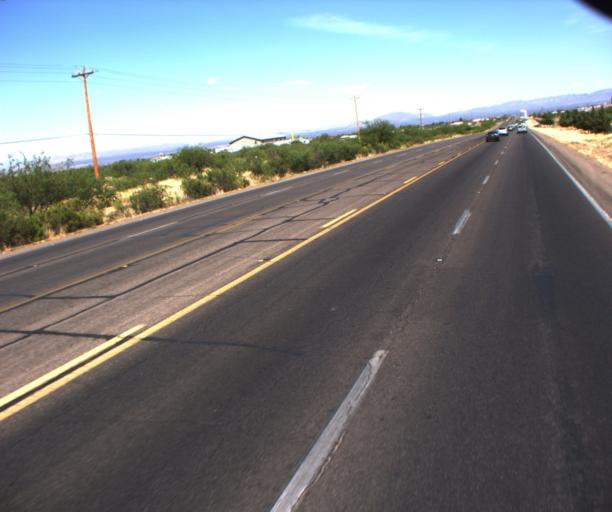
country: US
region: Arizona
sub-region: Cochise County
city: Sierra Vista
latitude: 31.5546
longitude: -110.2396
